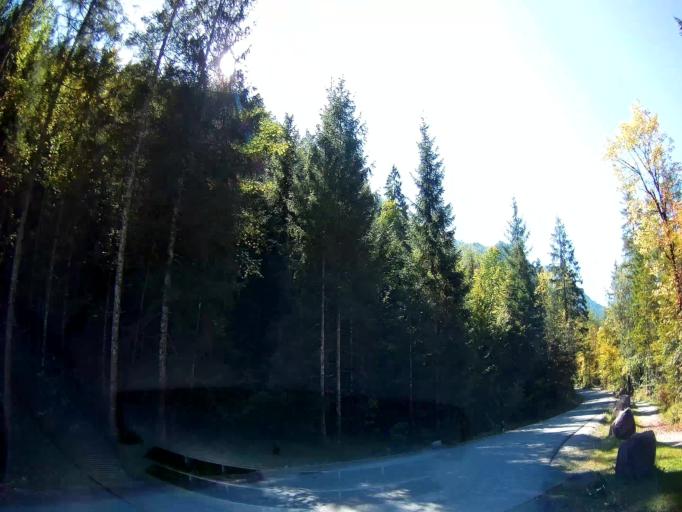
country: AT
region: Salzburg
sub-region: Politischer Bezirk Zell am See
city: Sankt Martin bei Lofer
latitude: 47.5264
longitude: 12.7142
